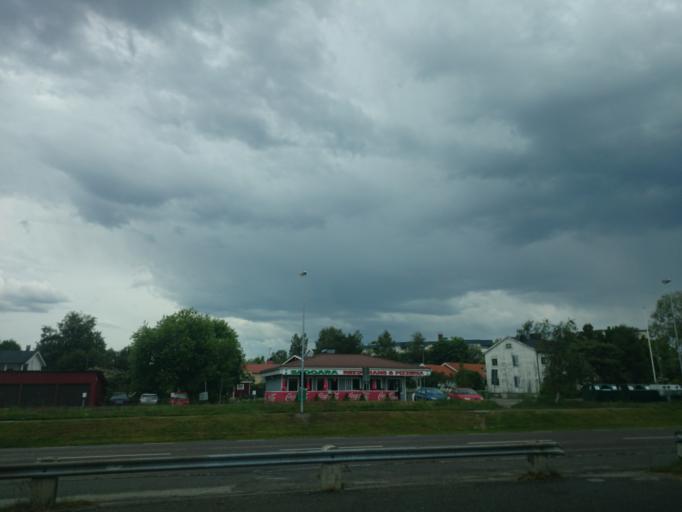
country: SE
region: Vaesternorrland
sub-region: Haernoesands Kommun
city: Haernoesand
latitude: 62.6271
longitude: 17.9221
